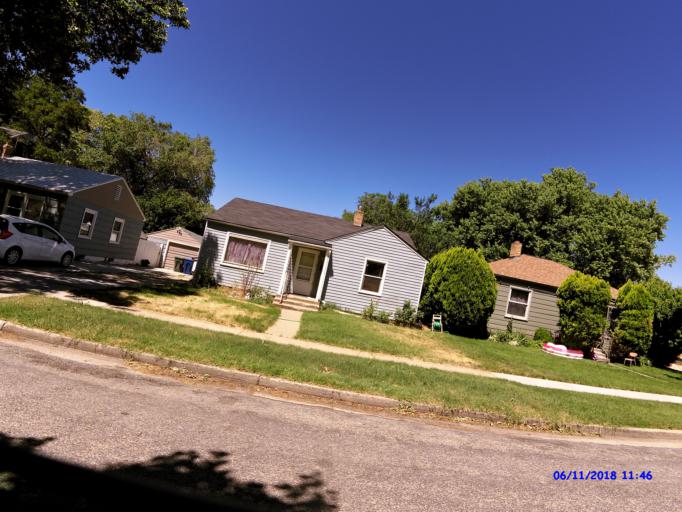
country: US
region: Utah
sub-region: Weber County
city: Ogden
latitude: 41.2320
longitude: -111.9494
